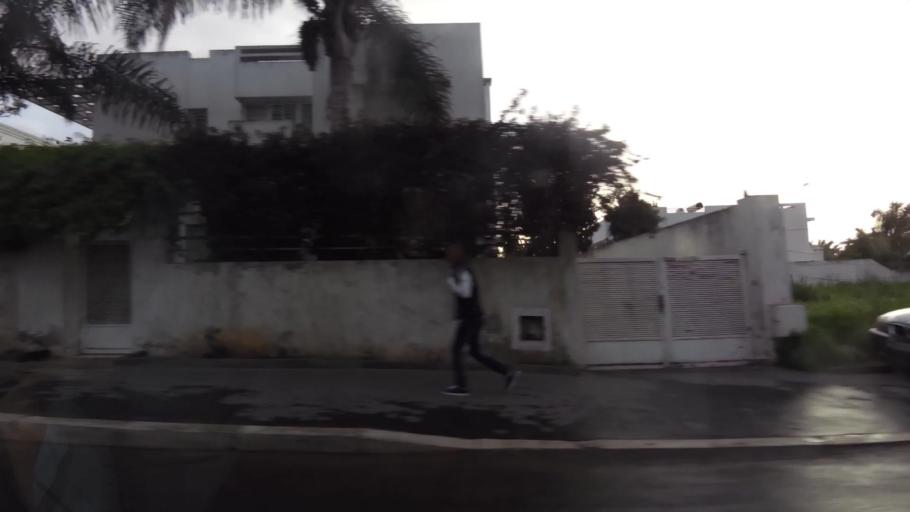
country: MA
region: Grand Casablanca
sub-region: Casablanca
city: Casablanca
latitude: 33.5799
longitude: -7.6747
